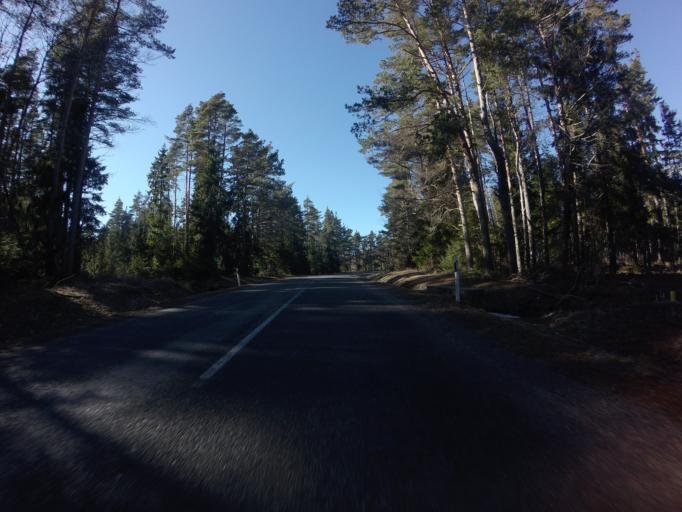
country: EE
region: Saare
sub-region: Kuressaare linn
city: Kuressaare
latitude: 58.5896
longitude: 22.6093
